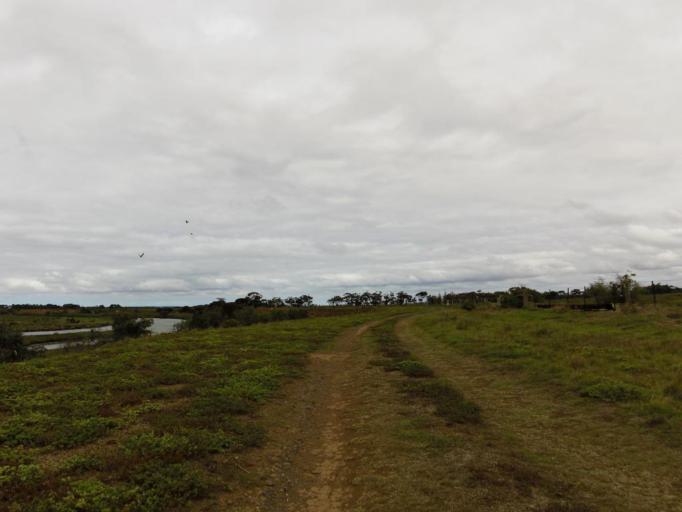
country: AU
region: Victoria
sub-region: Wyndham
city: Werribee
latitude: -37.9451
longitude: 144.6651
